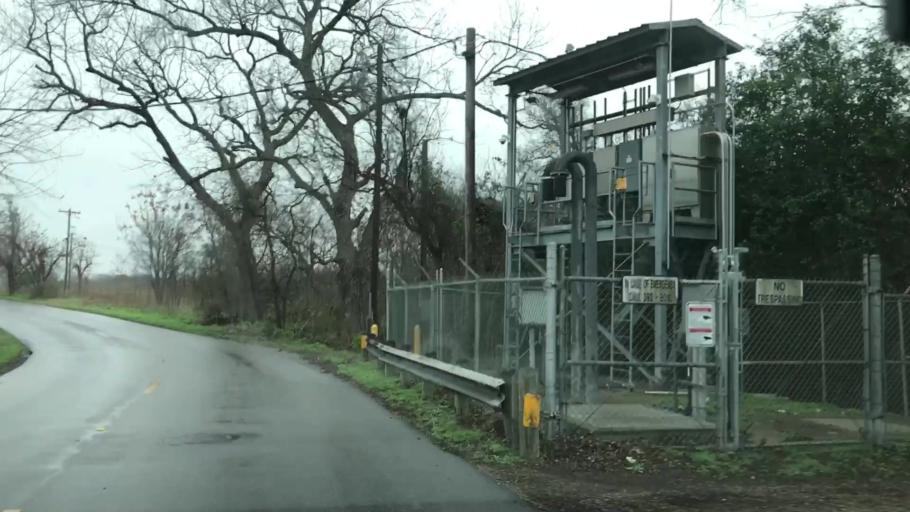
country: US
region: Texas
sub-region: Hays County
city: San Marcos
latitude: 29.8888
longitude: -97.9040
